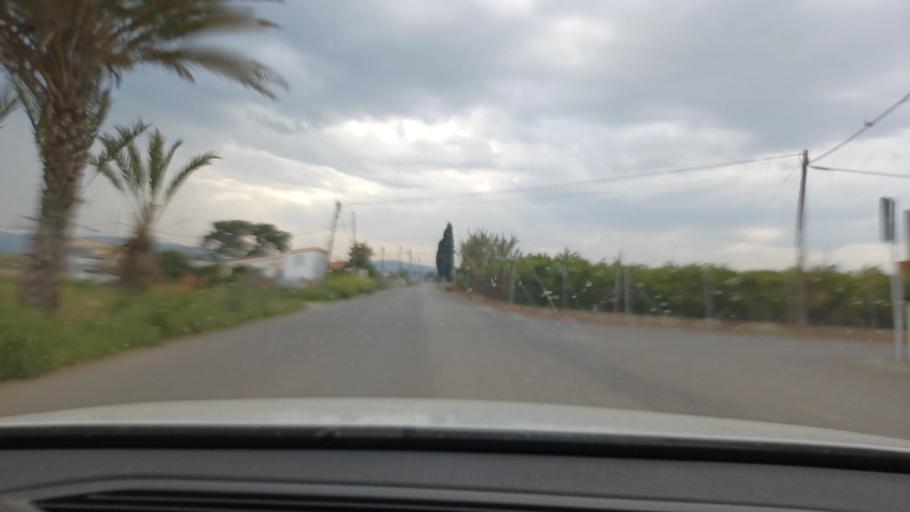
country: ES
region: Valencia
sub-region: Provincia de Castello
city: Benicarlo
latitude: 40.4038
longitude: 0.4074
